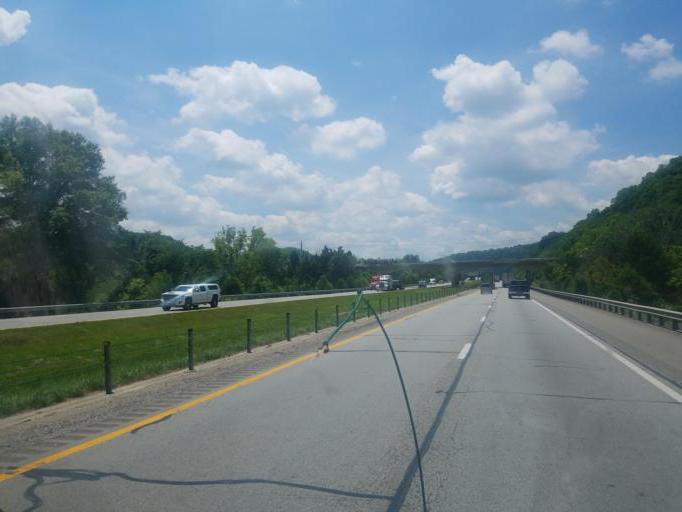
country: US
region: Kentucky
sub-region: Carroll County
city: Carrollton
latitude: 38.6321
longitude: -85.1382
